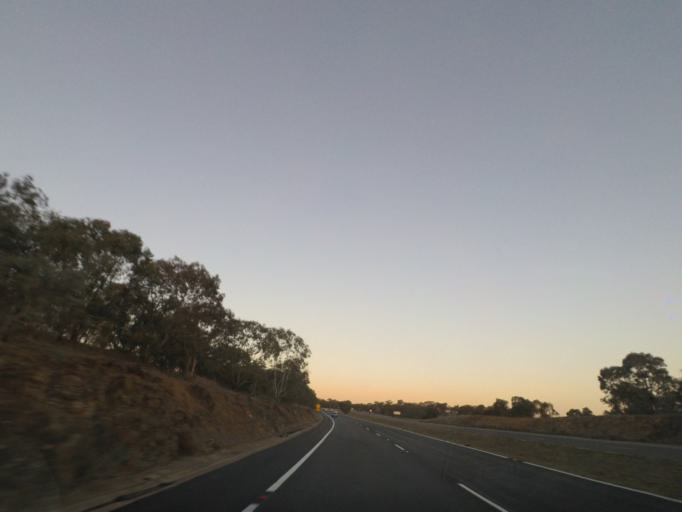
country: AU
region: Australian Capital Territory
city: Belconnen
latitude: -35.1774
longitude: 149.0664
